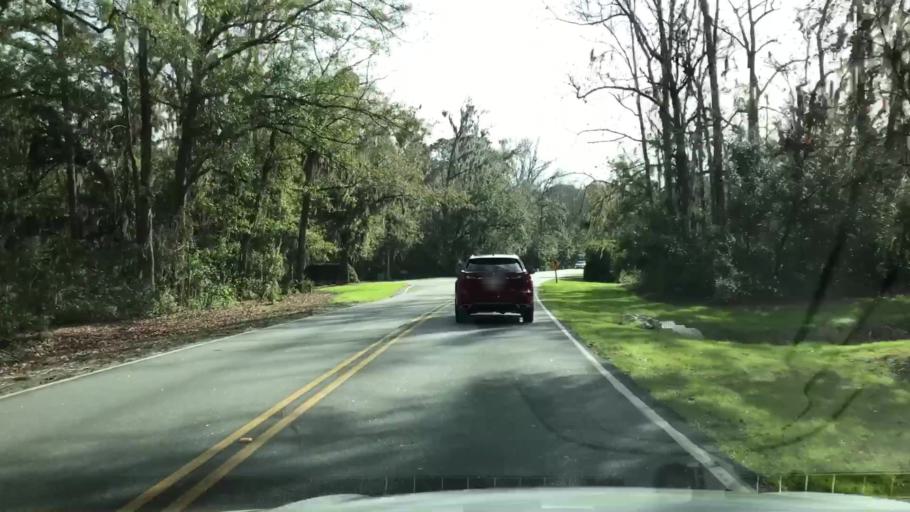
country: US
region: South Carolina
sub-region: Beaufort County
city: Hilton Head Island
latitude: 32.2236
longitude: -80.7230
